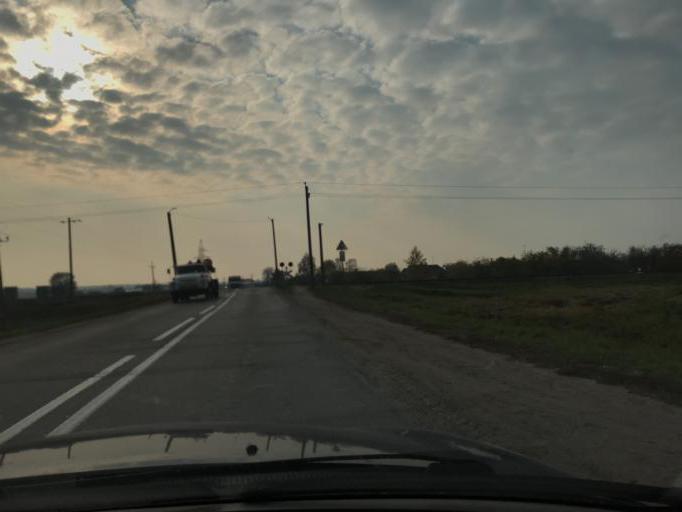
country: BY
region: Grodnenskaya
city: Lida
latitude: 53.8584
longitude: 25.3261
